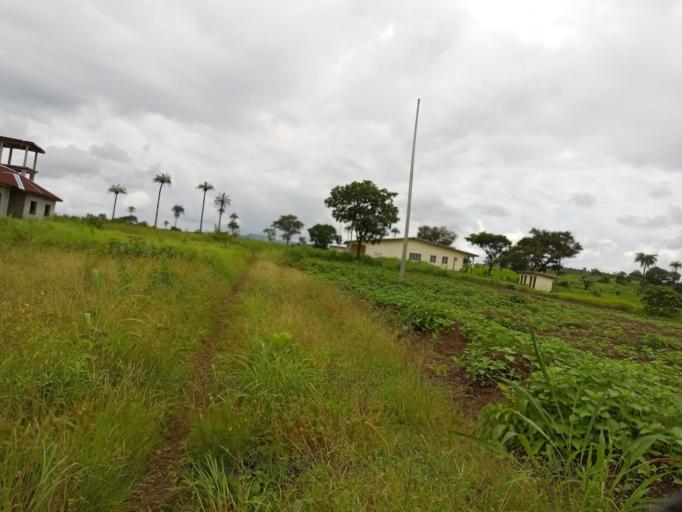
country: SL
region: Northern Province
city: Kamakwie
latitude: 9.5042
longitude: -12.2565
